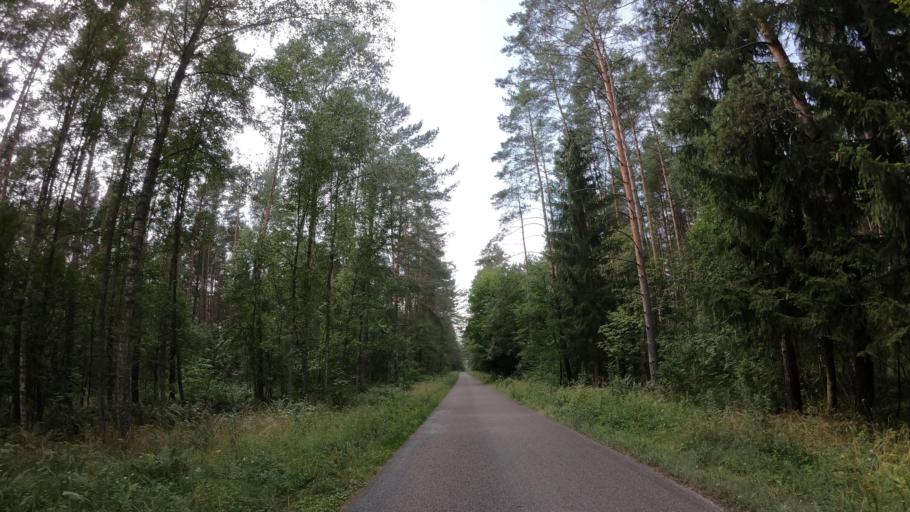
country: PL
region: West Pomeranian Voivodeship
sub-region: Powiat walecki
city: Tuczno
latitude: 53.2305
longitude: 16.1004
